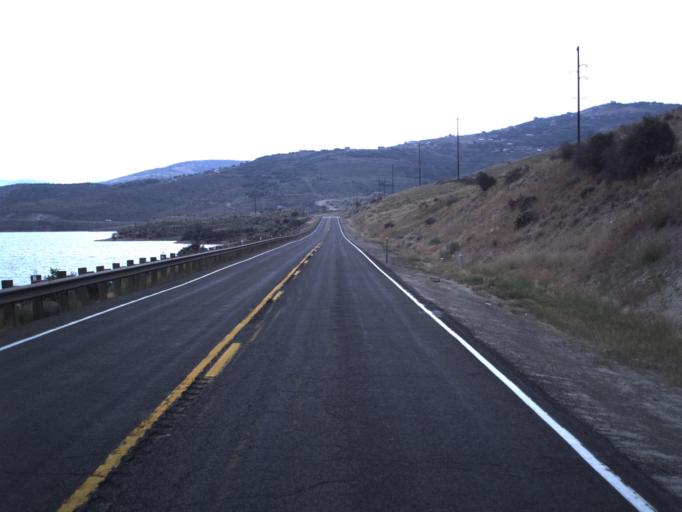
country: US
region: Utah
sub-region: Summit County
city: Oakley
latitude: 40.7833
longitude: -111.4089
